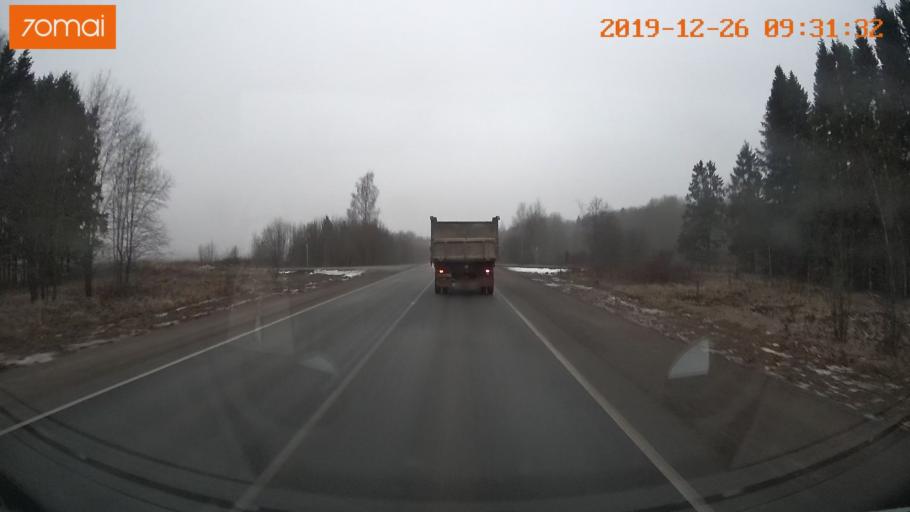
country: RU
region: Vologda
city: Gryazovets
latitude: 59.0699
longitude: 40.1269
